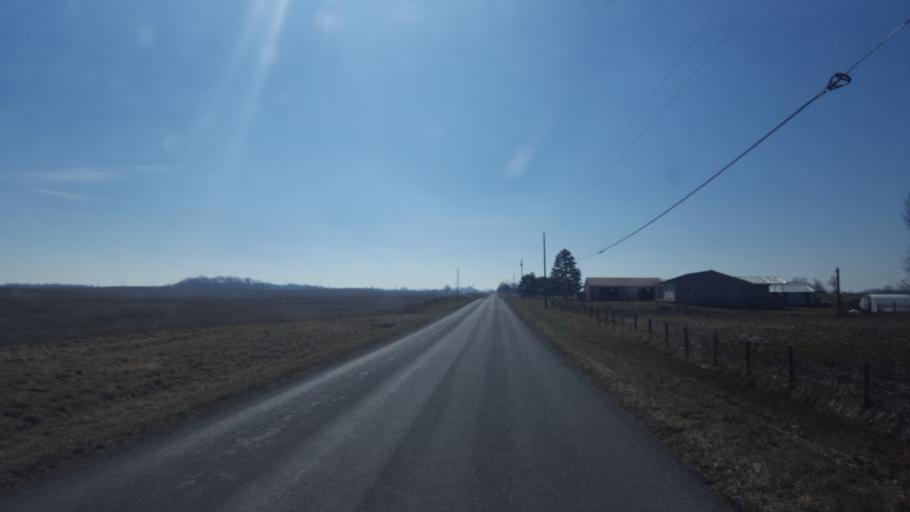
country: US
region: Ohio
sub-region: Huron County
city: Greenwich
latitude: 41.0000
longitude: -82.5827
